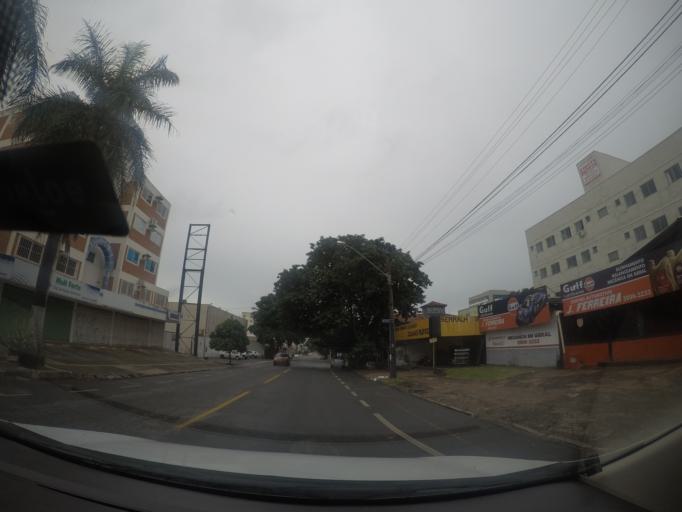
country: BR
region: Goias
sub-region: Goiania
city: Goiania
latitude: -16.7104
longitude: -49.2837
